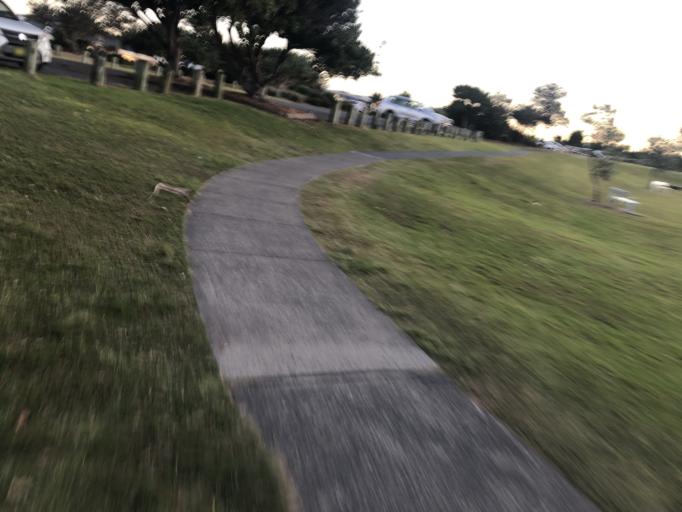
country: AU
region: New South Wales
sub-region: Coffs Harbour
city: Coffs Harbour
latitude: -30.3049
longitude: 153.1395
